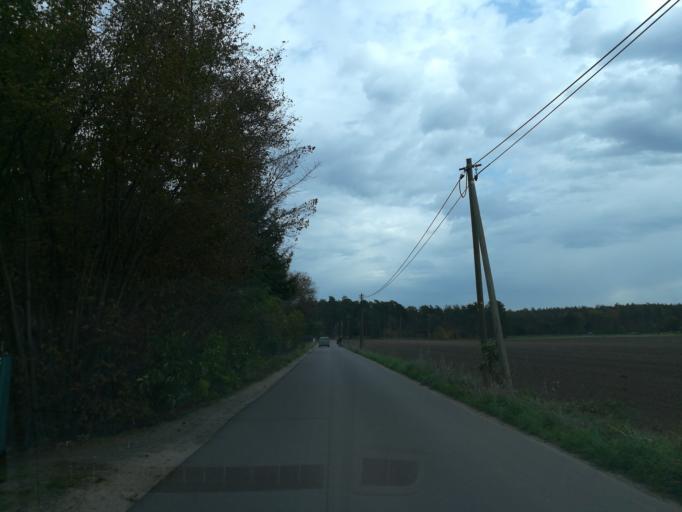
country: DE
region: Saxony-Anhalt
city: Plotzky
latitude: 52.0610
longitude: 11.8041
